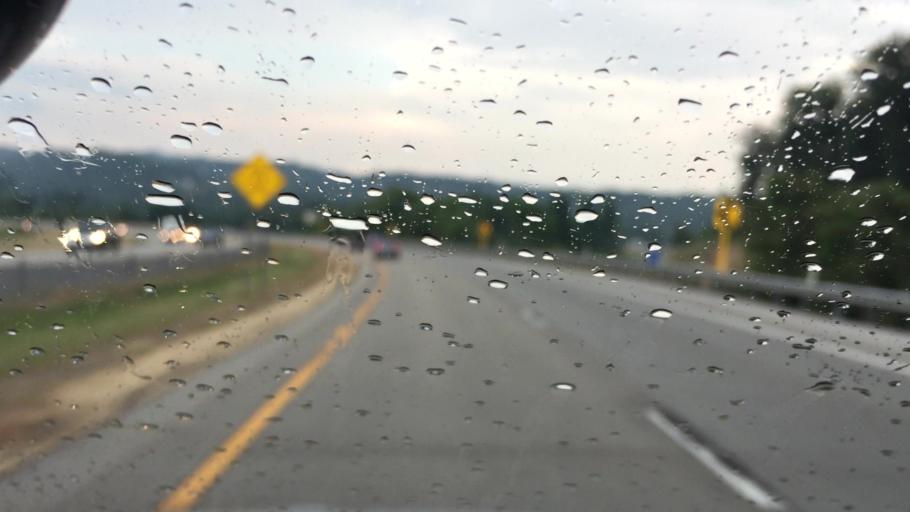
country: US
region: West Virginia
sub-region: Monongalia County
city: Cheat Lake
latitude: 39.6702
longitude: -79.8485
